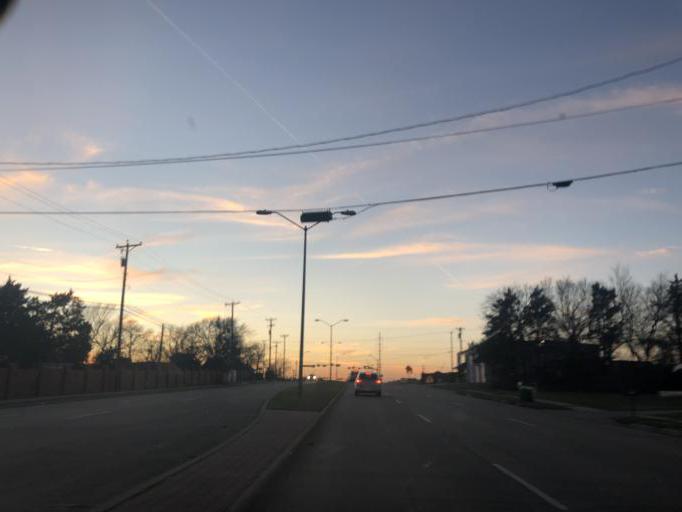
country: US
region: Texas
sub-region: Dallas County
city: Cedar Hill
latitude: 32.6044
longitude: -96.9282
